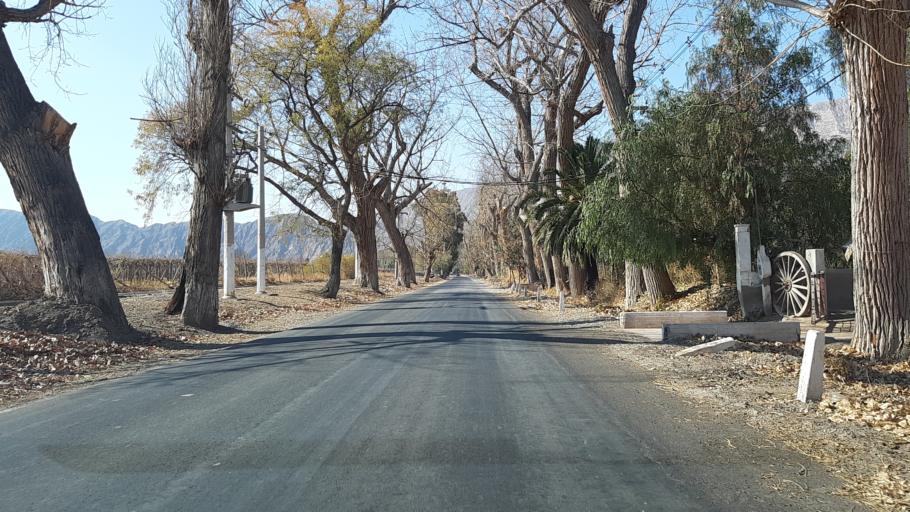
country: AR
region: San Juan
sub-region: Departamento de Zonda
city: Zonda
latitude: -31.5604
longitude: -68.7298
